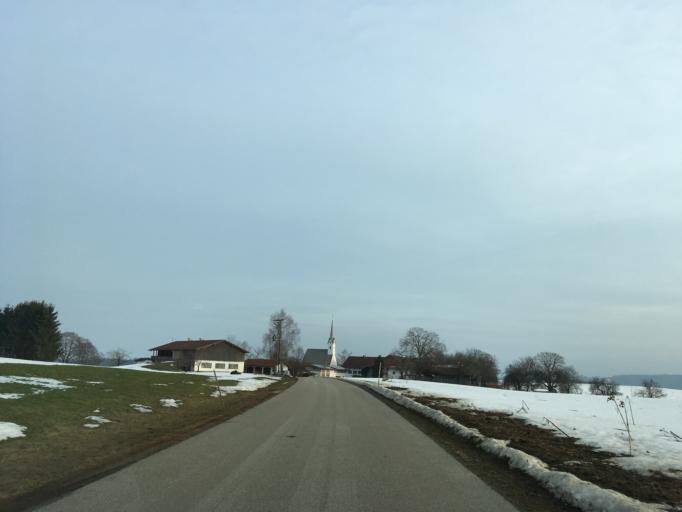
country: DE
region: Bavaria
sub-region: Upper Bavaria
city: Halfing
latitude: 47.9353
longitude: 12.2909
